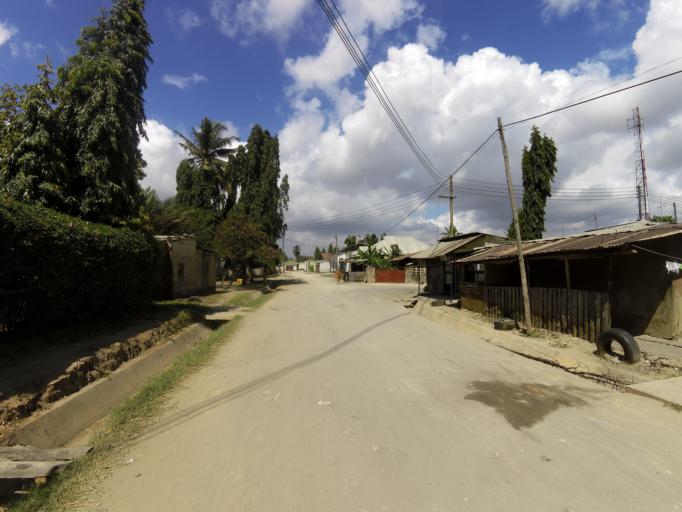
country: TZ
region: Dar es Salaam
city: Magomeni
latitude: -6.7885
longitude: 39.2586
